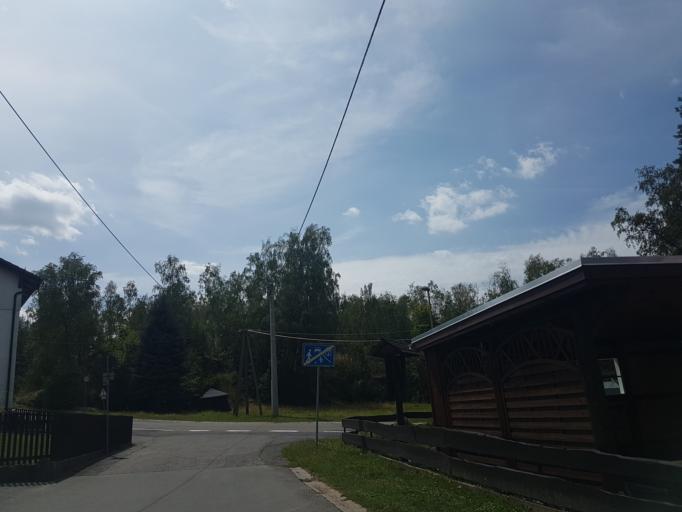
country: DE
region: Saxony
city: Freiberg
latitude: 50.8875
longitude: 13.3570
